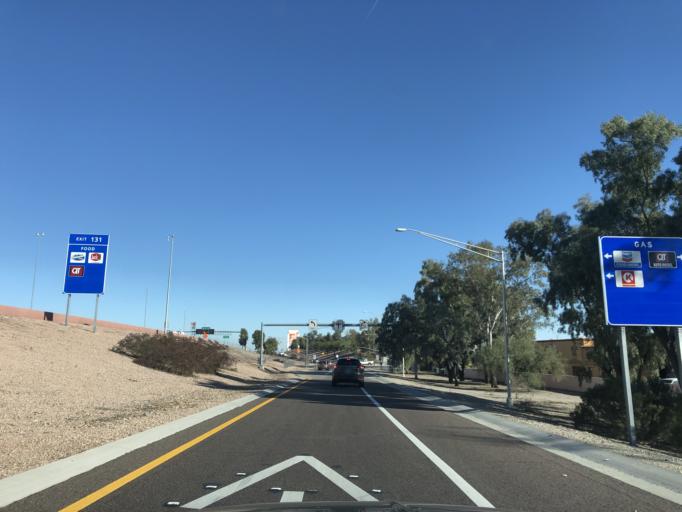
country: US
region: Arizona
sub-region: Maricopa County
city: Avondale
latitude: 33.4574
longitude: -112.3431
